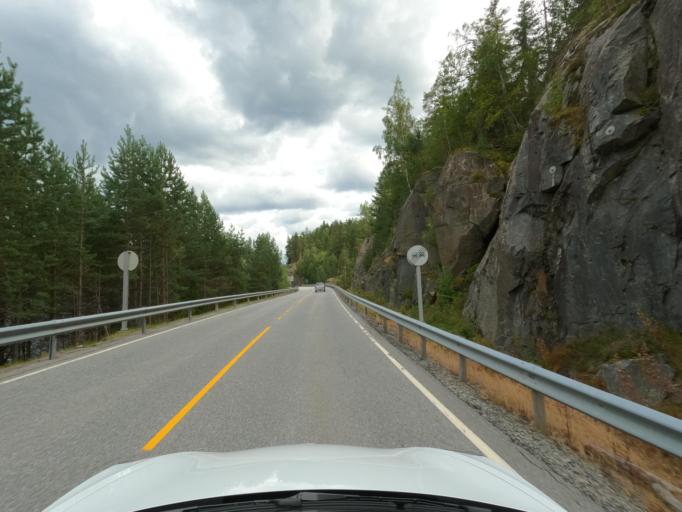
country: NO
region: Telemark
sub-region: Hjartdal
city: Sauland
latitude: 59.8694
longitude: 8.9286
